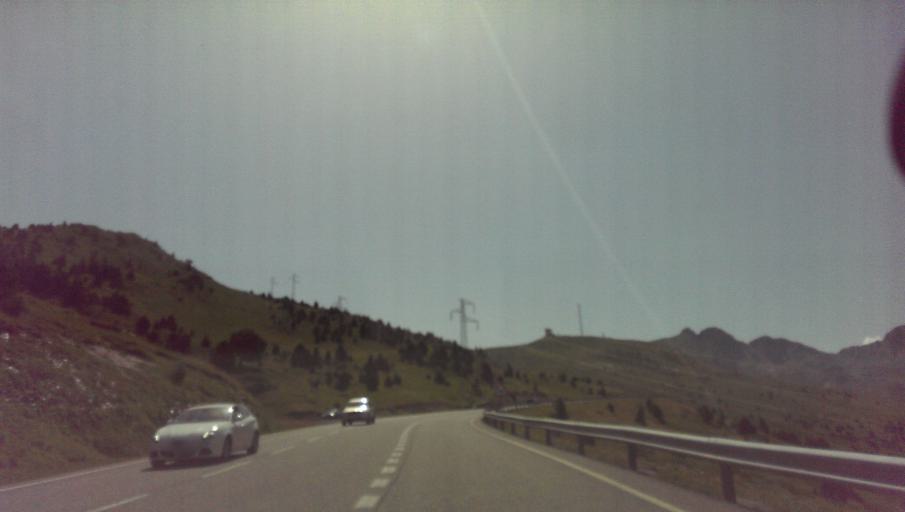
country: AD
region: Encamp
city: Pas de la Casa
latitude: 42.5464
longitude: 1.7064
